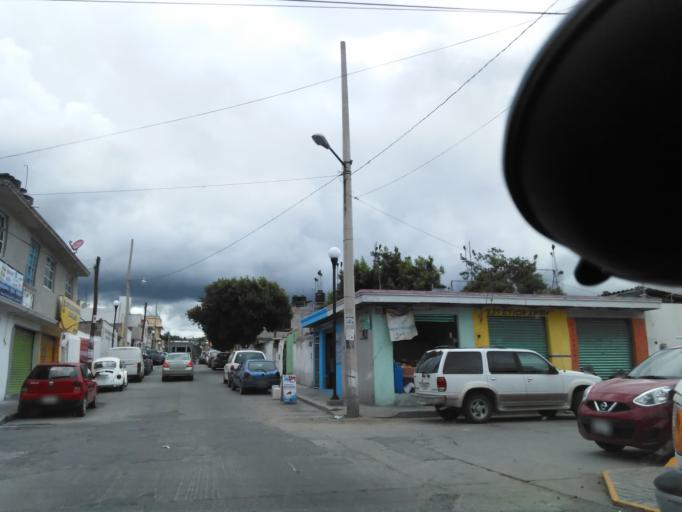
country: MX
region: Hidalgo
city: Tula de Allende
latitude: 20.0586
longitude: -99.3408
